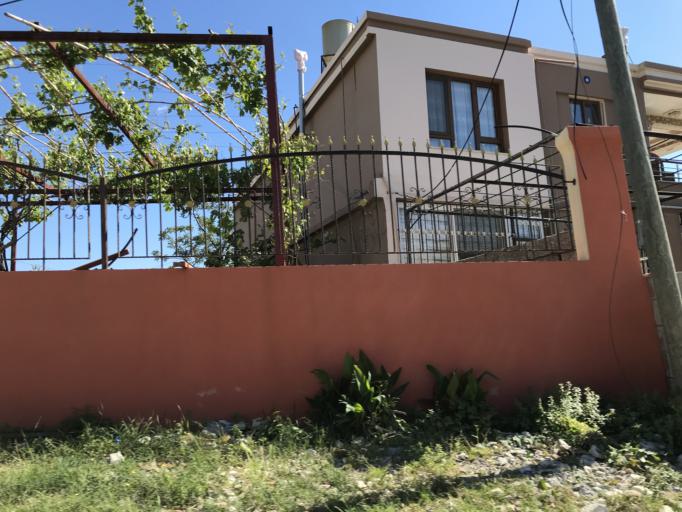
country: TR
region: Hatay
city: Samandag
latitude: 36.1134
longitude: 35.9357
